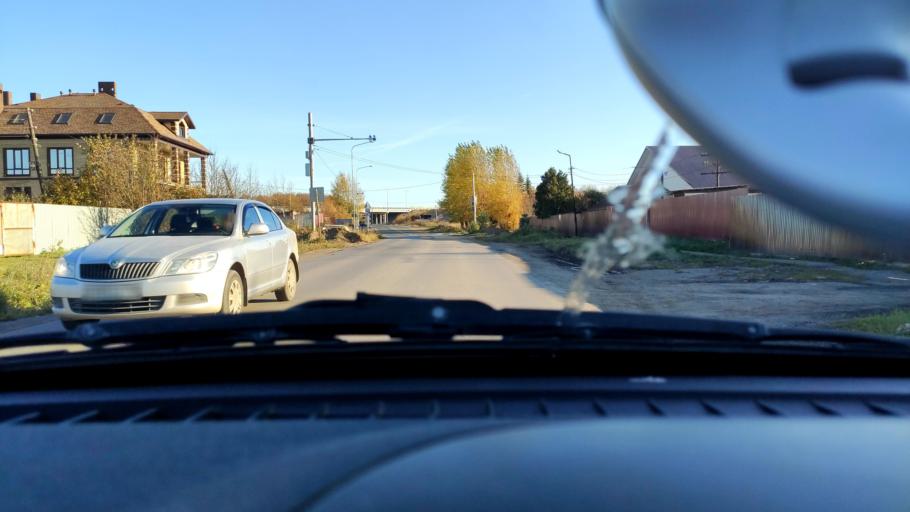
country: RU
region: Perm
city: Froly
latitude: 57.8817
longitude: 56.2621
